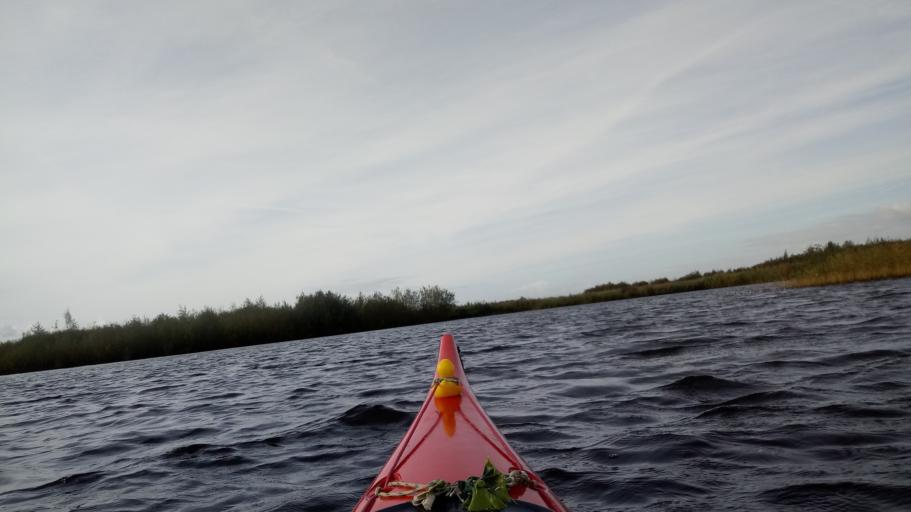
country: NL
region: Overijssel
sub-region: Gemeente Steenwijkerland
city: Sint Jansklooster
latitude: 52.6935
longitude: 6.0232
